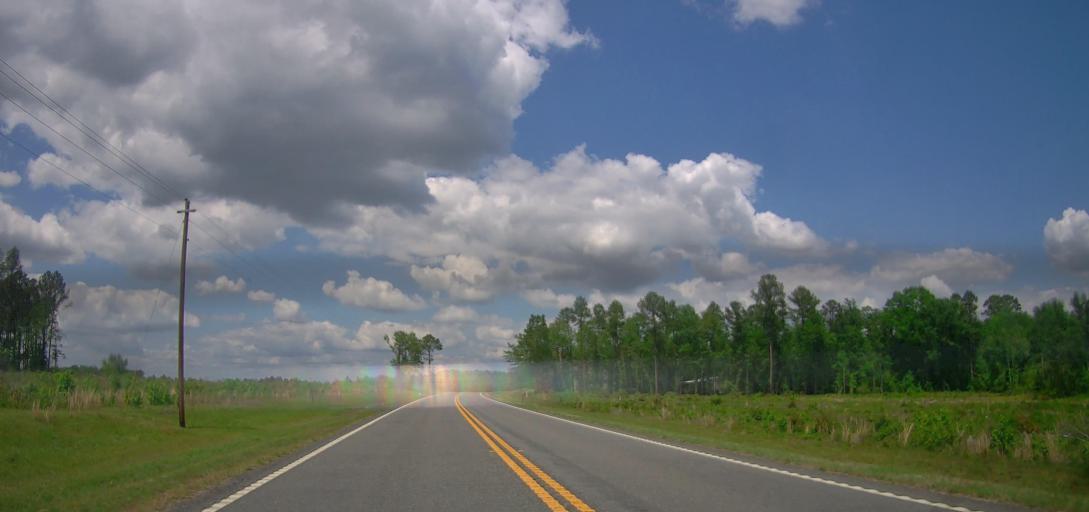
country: US
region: Georgia
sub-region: Treutlen County
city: Soperton
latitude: 32.4117
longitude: -82.6080
